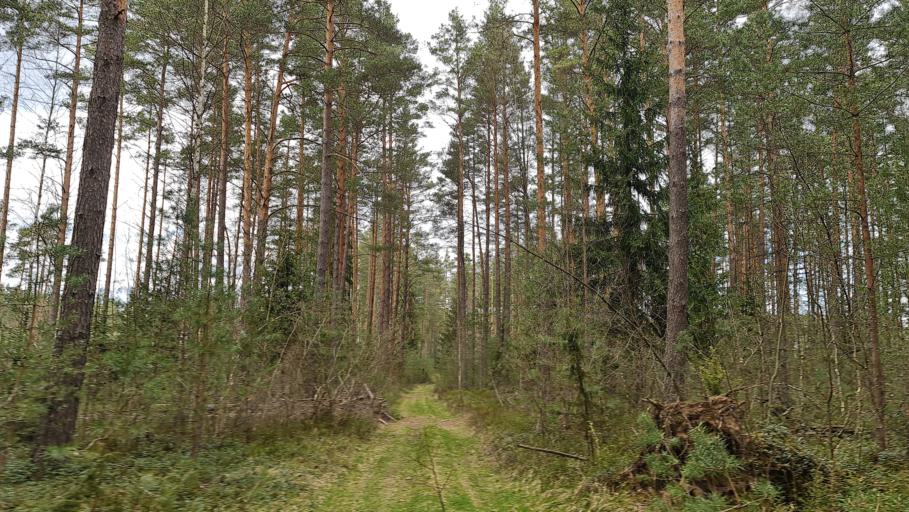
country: BY
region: Vitebsk
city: Byahoml'
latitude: 54.7369
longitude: 28.0327
